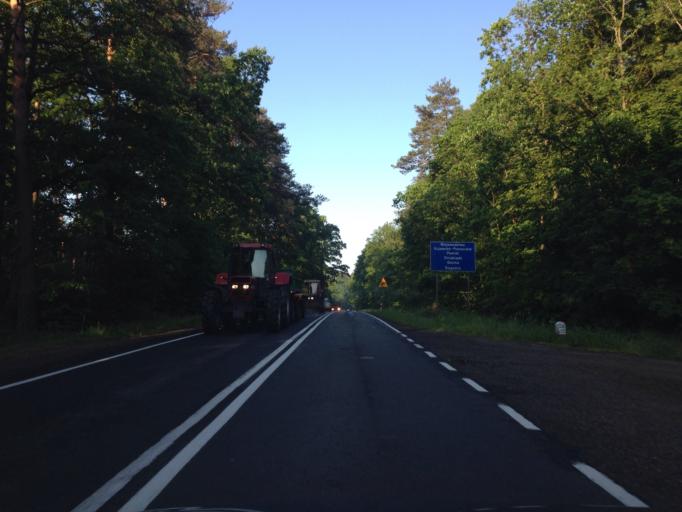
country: PL
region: Pomeranian Voivodeship
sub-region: Powiat kwidzynski
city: Gardeja
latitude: 53.5872
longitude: 18.9072
